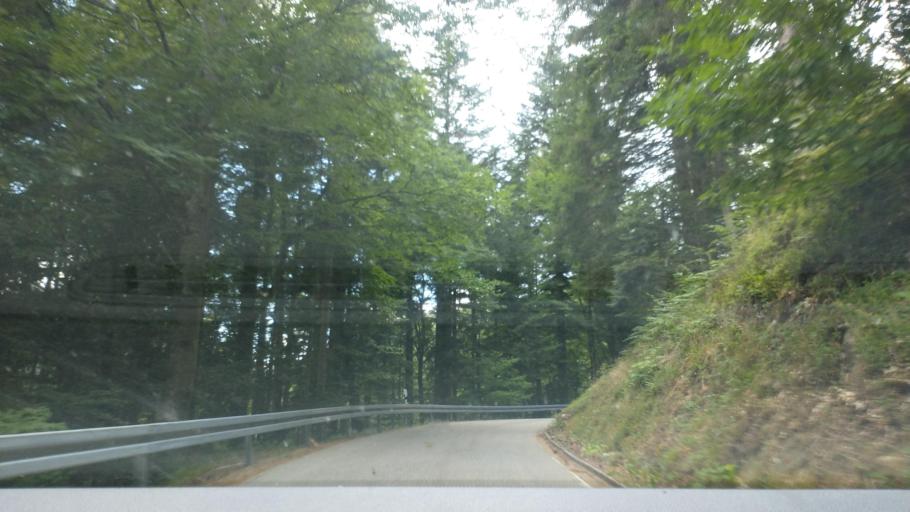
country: DE
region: Baden-Wuerttemberg
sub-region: Freiburg Region
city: Oppenau
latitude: 48.4332
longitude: 8.1341
